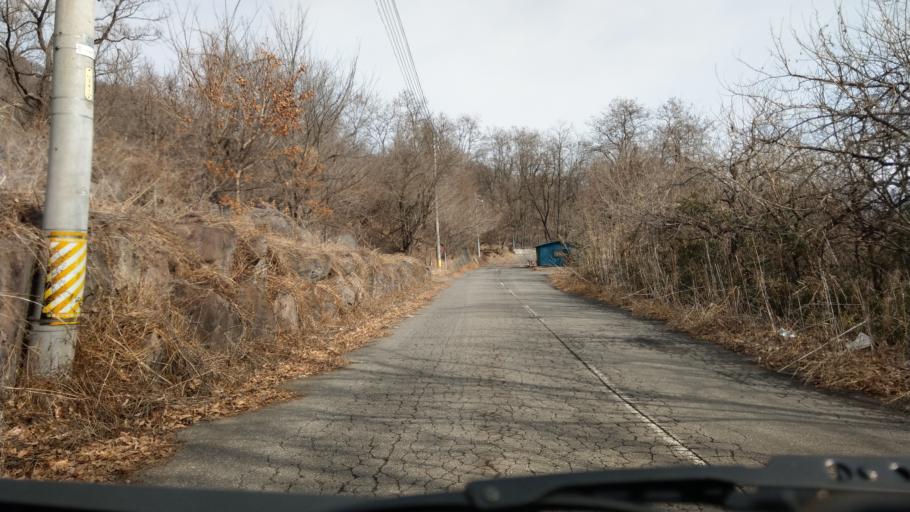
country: JP
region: Nagano
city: Komoro
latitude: 36.2859
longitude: 138.4070
